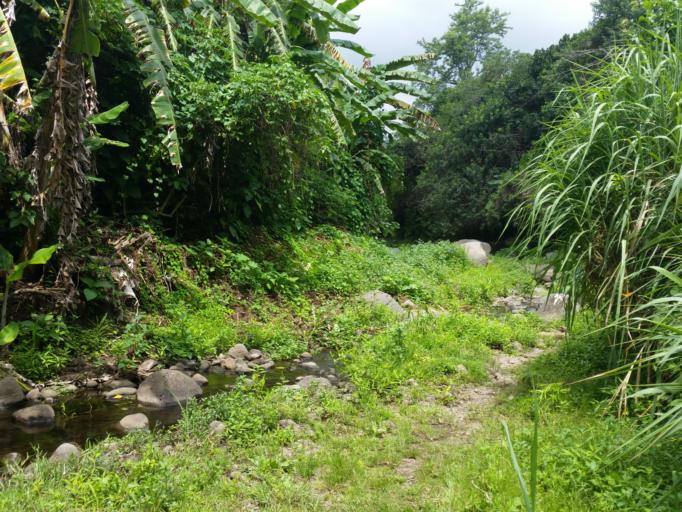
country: RE
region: Reunion
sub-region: Reunion
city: L'Entre-Deux
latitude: -21.2521
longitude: 55.4669
